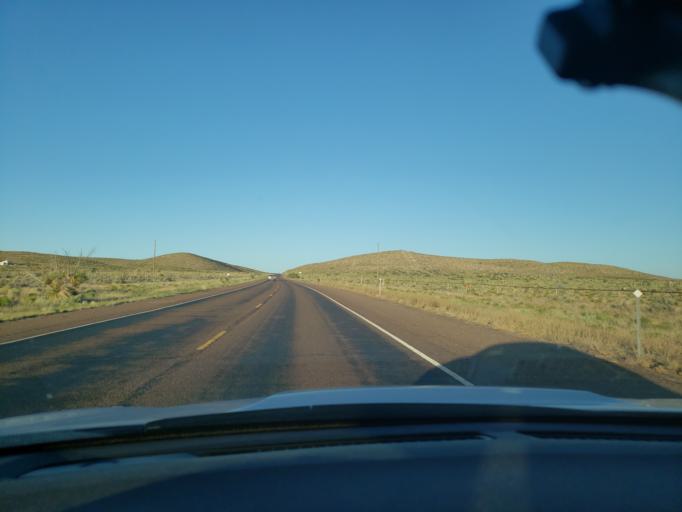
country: US
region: Texas
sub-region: El Paso County
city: Homestead Meadows South
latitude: 31.8267
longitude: -105.9026
